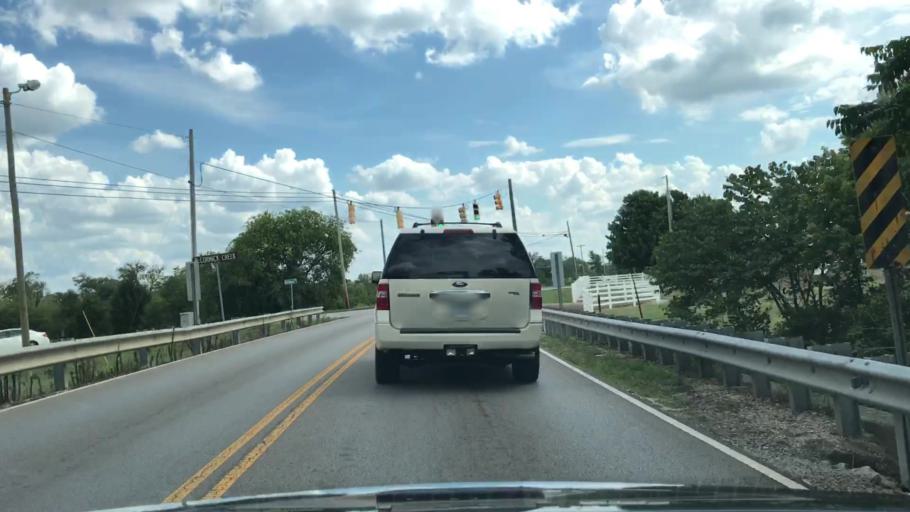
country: US
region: Tennessee
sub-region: Maury County
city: Spring Hill
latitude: 35.7411
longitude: -86.9250
